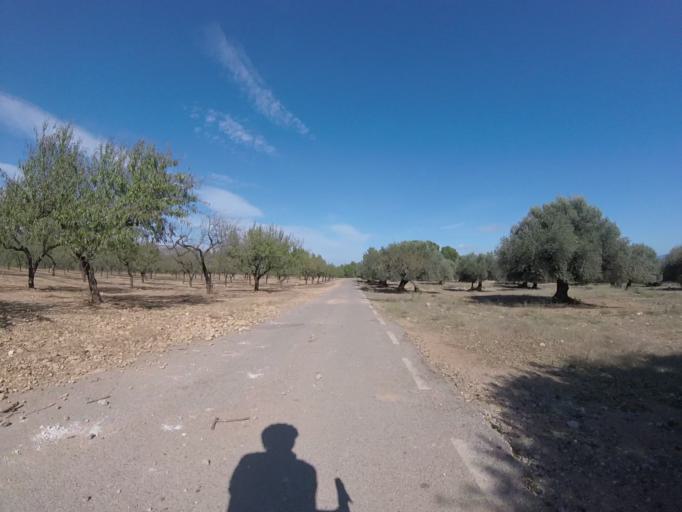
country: ES
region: Valencia
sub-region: Provincia de Castello
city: Sarratella
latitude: 40.2739
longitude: 0.0606
